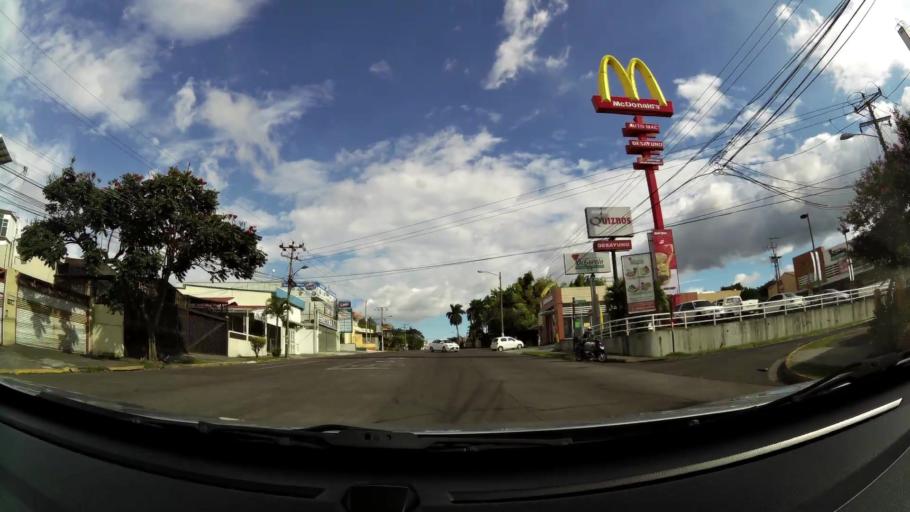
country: CR
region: San Jose
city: San Rafael
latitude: 9.9433
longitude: -84.1270
